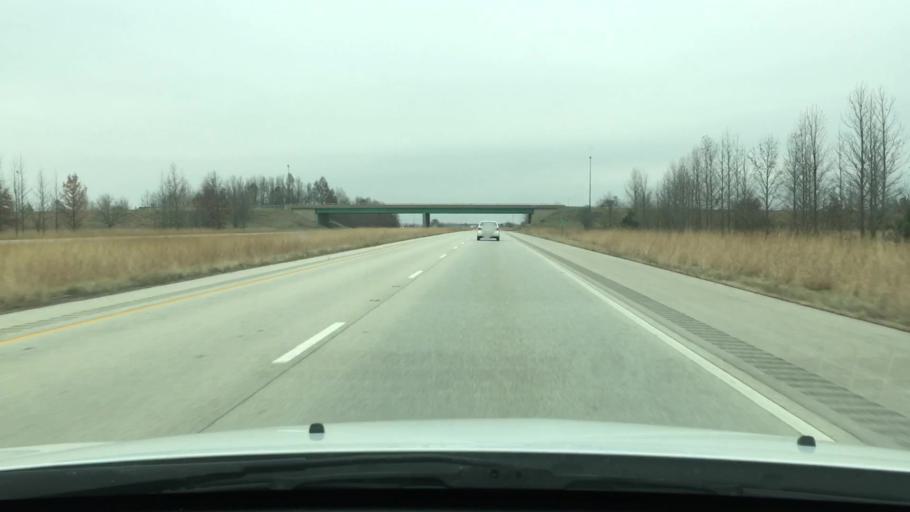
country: US
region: Illinois
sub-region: Sangamon County
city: New Berlin
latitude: 39.7400
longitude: -89.9268
